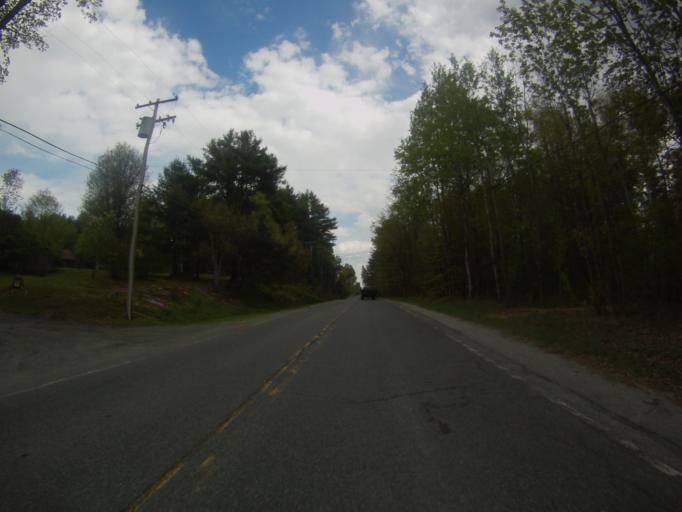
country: US
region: New York
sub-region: Essex County
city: Mineville
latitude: 44.0715
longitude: -73.5225
